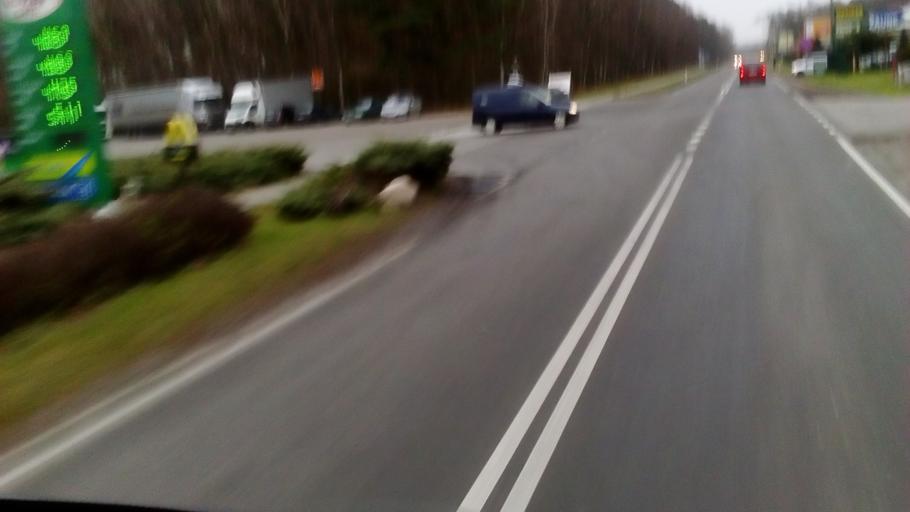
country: PL
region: West Pomeranian Voivodeship
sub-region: Powiat policki
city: Dobra
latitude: 53.4481
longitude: 14.3932
